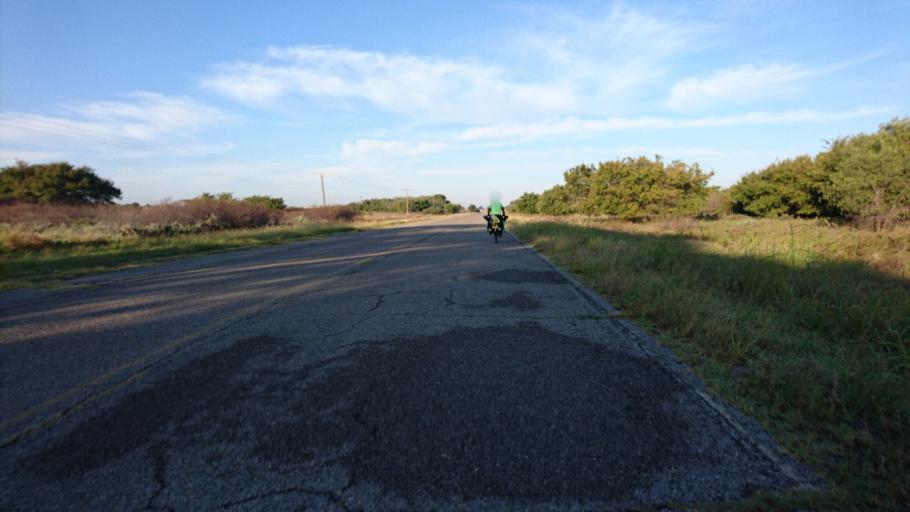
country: US
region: Oklahoma
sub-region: Beckham County
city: Sayre
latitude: 35.2621
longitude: -99.7138
